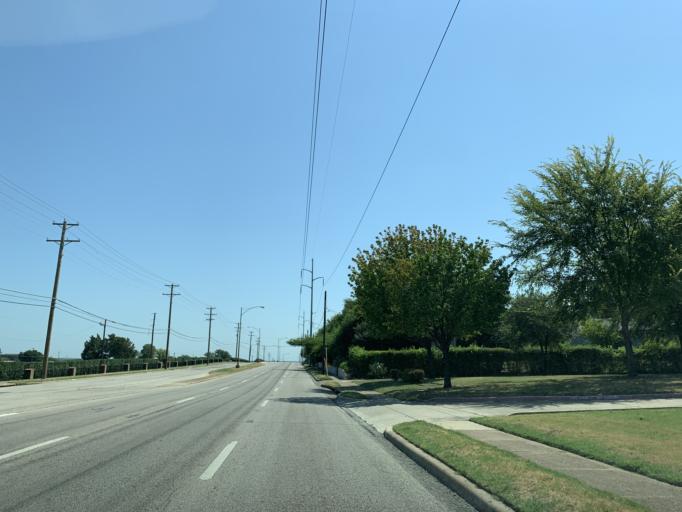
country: US
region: Texas
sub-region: Dallas County
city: Hutchins
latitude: 32.6745
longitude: -96.7591
